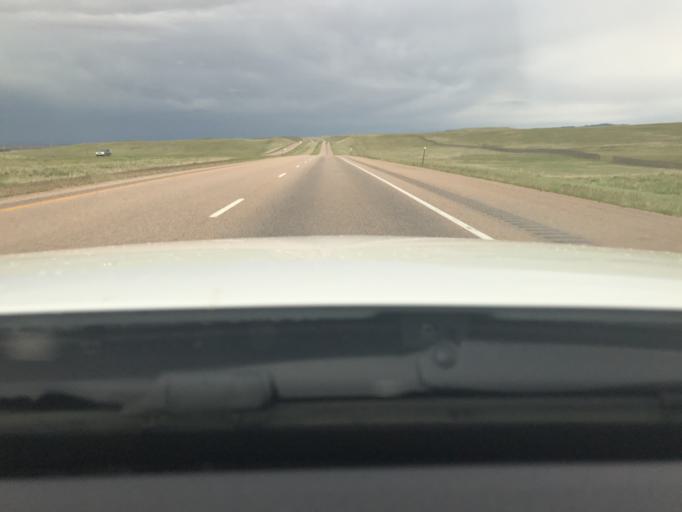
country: US
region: Wyoming
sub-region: Natrona County
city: Evansville
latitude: 42.8391
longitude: -106.1320
